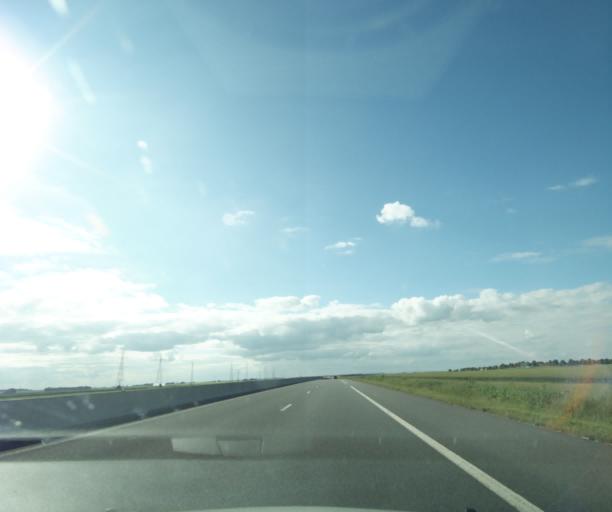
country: FR
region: Centre
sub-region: Departement d'Eure-et-Loir
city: Voves
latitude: 48.3408
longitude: 1.6354
